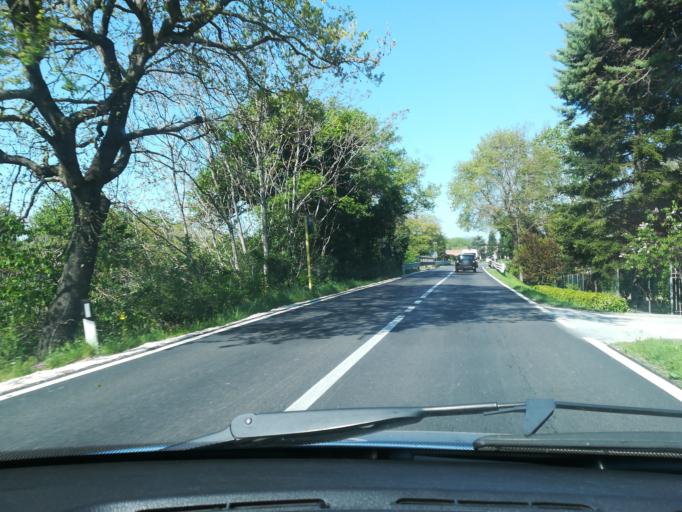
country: IT
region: The Marches
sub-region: Provincia di Macerata
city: Villa Potenza
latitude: 43.3241
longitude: 13.4153
